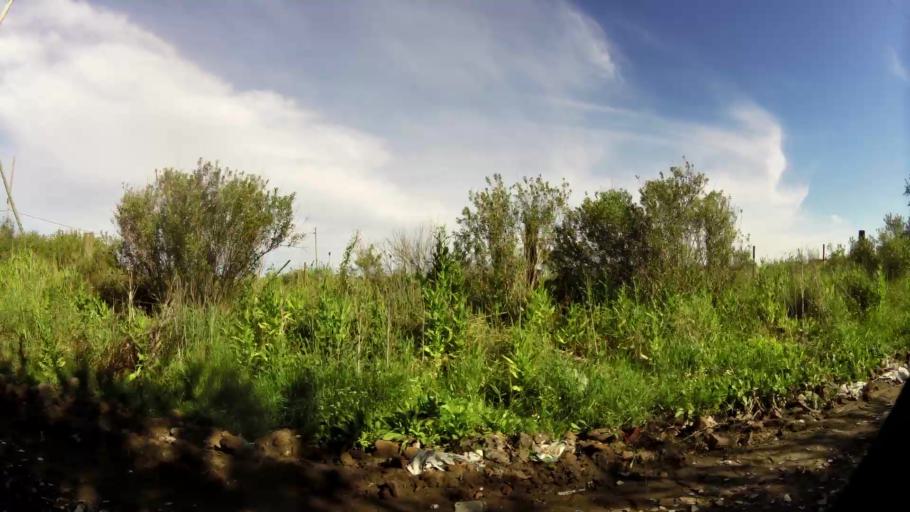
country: AR
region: Buenos Aires
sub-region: Partido de Almirante Brown
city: Adrogue
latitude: -34.8263
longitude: -58.3385
